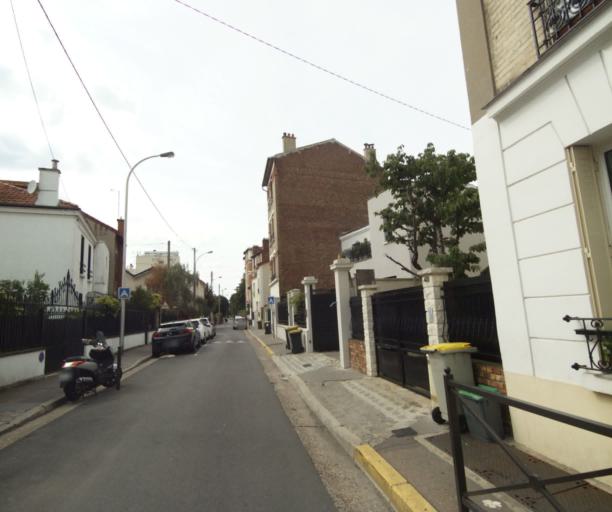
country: FR
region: Ile-de-France
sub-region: Departement des Hauts-de-Seine
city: Bois-Colombes
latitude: 48.9209
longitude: 2.2745
